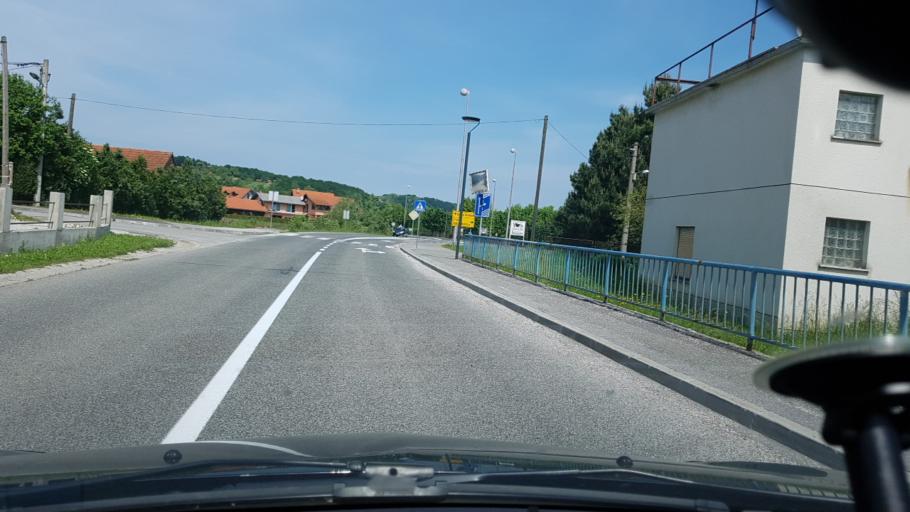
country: HR
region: Krapinsko-Zagorska
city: Marija Bistrica
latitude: 46.0045
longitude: 16.1103
